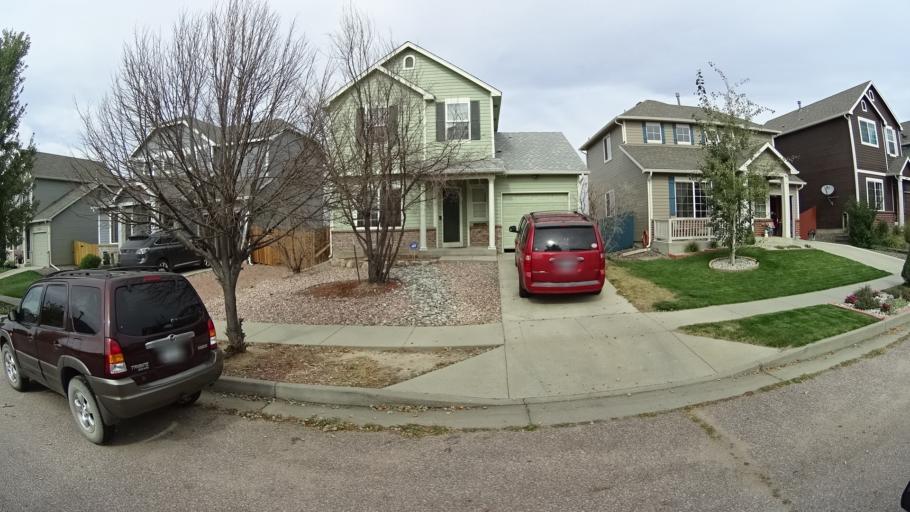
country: US
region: Colorado
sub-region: El Paso County
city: Cimarron Hills
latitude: 38.9225
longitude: -104.7162
